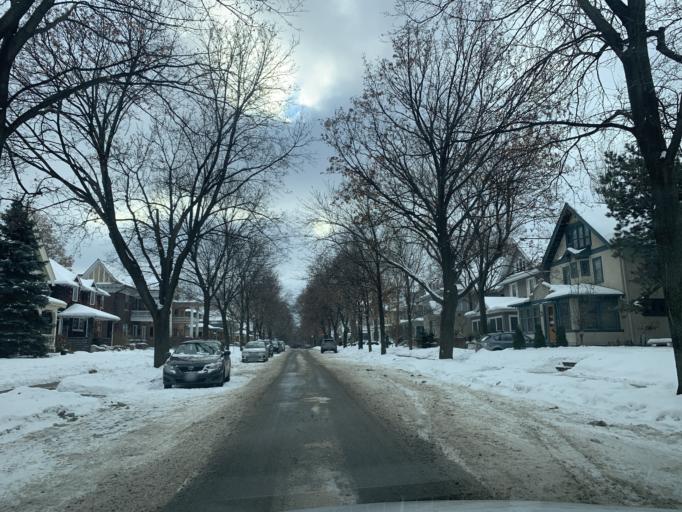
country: US
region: Minnesota
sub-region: Hennepin County
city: Minneapolis
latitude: 44.9603
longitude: -93.2982
